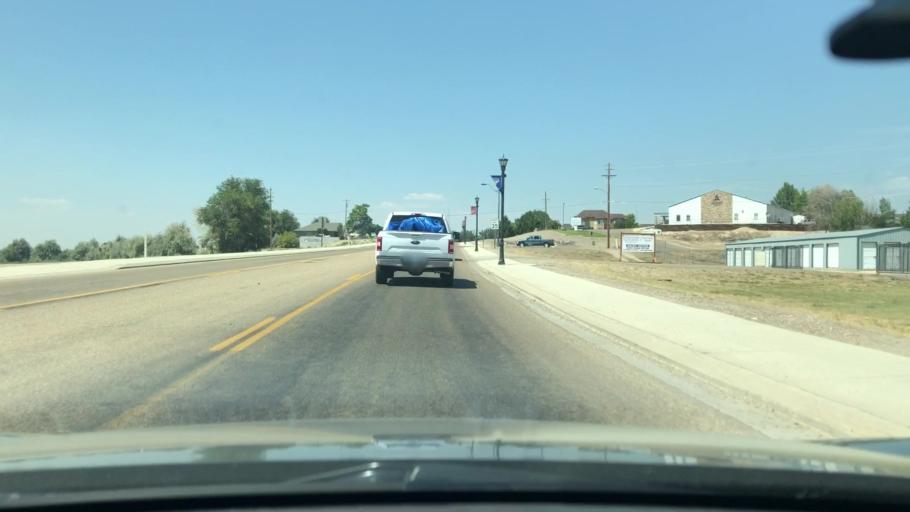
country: US
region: Idaho
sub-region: Canyon County
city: Parma
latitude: 43.7876
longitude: -116.9473
